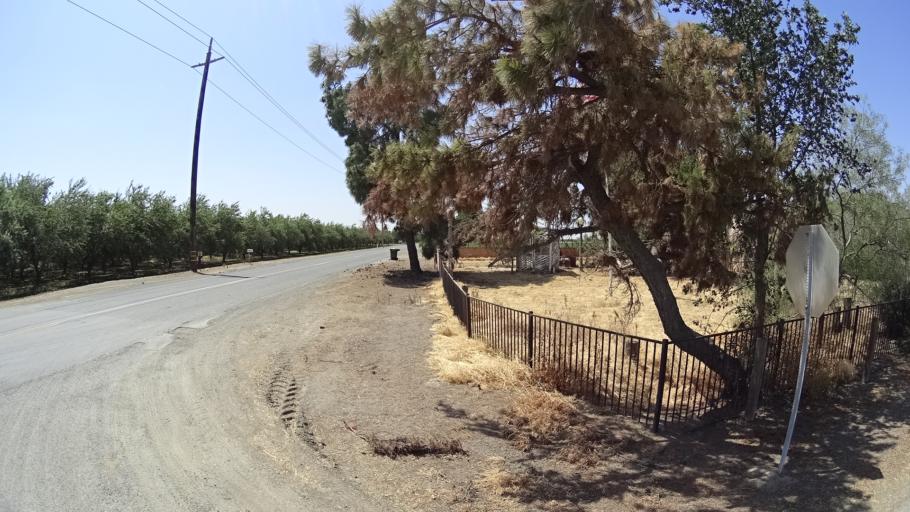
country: US
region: California
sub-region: Kings County
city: Home Garden
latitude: 36.2840
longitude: -119.5832
